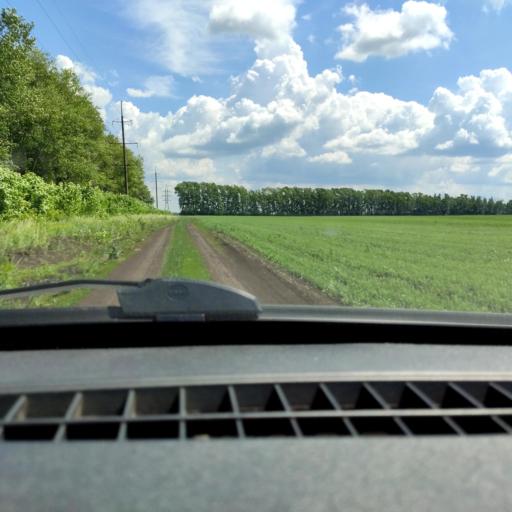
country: RU
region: Bashkortostan
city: Kabakovo
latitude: 54.5200
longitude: 56.0772
